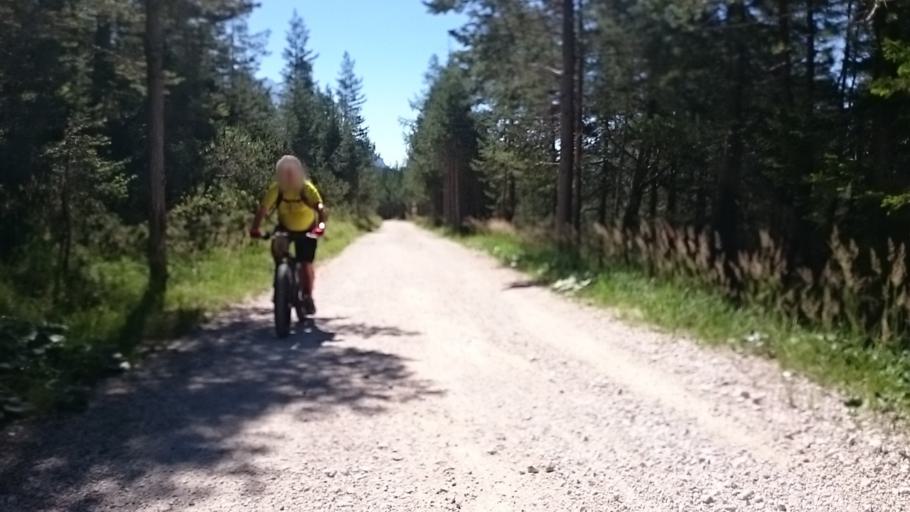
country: IT
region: Veneto
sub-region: Provincia di Belluno
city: Cortina d'Ampezzo
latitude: 46.5770
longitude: 12.1186
